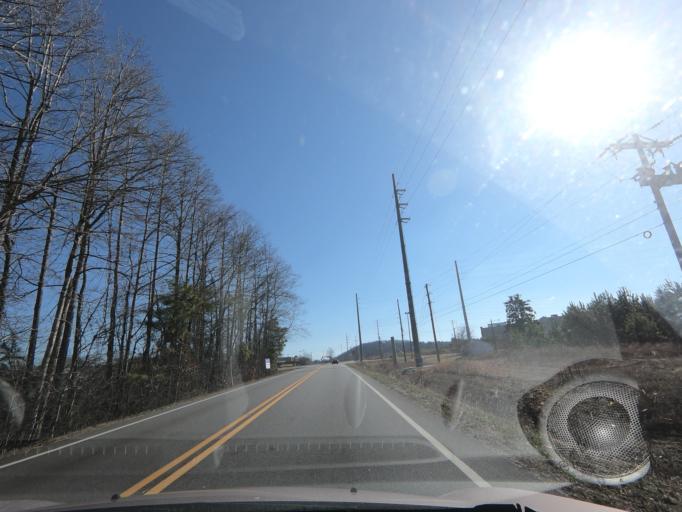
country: US
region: Georgia
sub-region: Dawson County
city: Dawsonville
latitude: 34.3546
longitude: -84.0533
